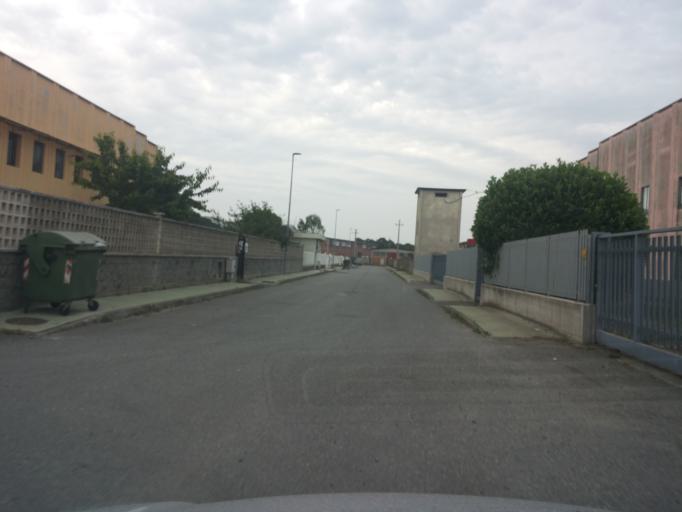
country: IT
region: Piedmont
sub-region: Provincia di Biella
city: Cavaglia
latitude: 45.3872
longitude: 8.1265
